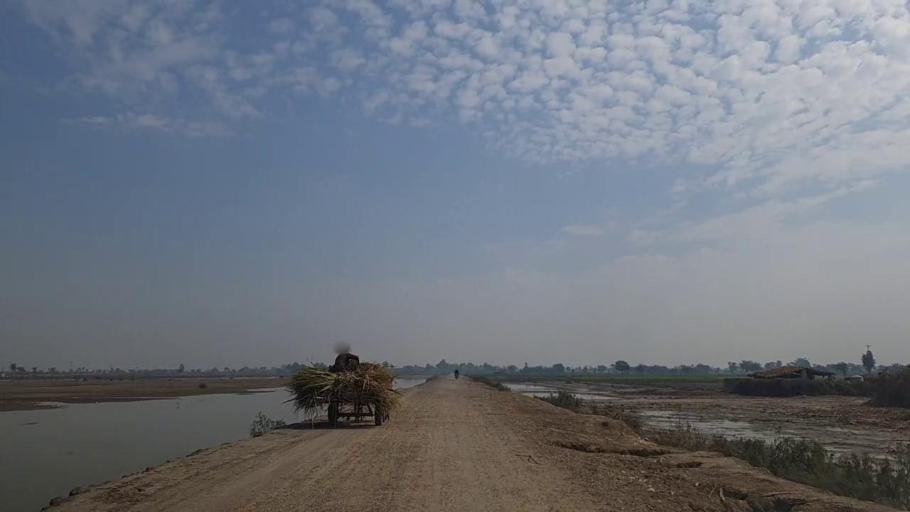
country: PK
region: Sindh
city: Daur
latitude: 26.3840
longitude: 68.3834
